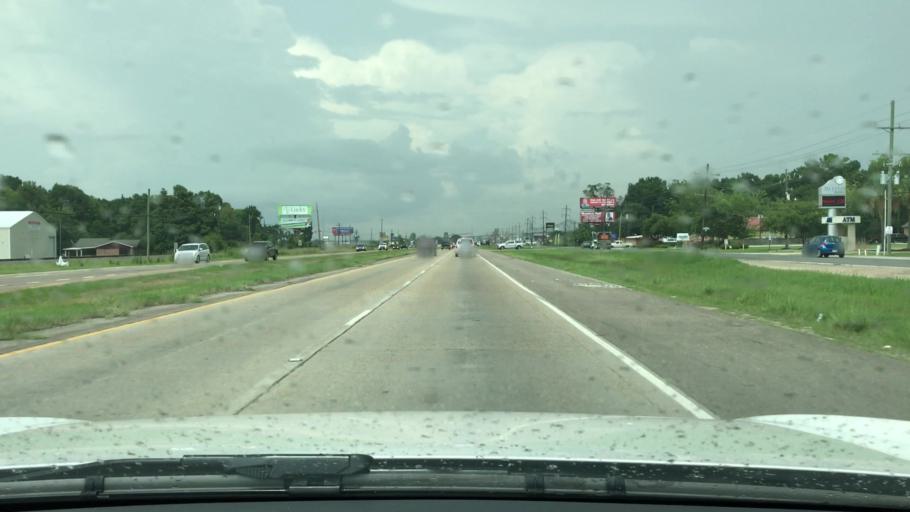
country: US
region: Louisiana
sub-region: West Baton Rouge Parish
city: Brusly
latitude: 30.4148
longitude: -91.2241
